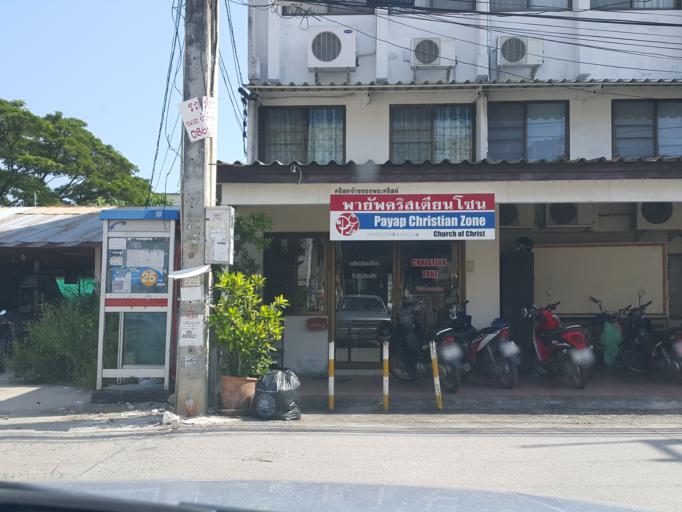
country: TH
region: Chiang Mai
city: Chiang Mai
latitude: 18.7937
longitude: 99.0294
